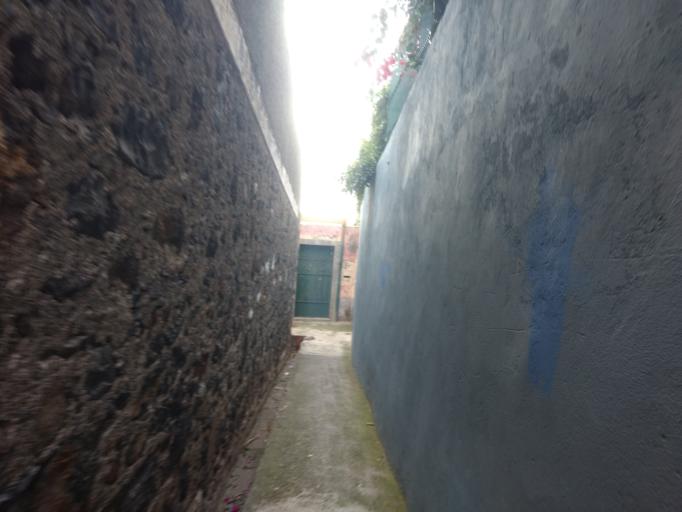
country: PT
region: Madeira
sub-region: Funchal
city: Funchal
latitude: 32.6466
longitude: -16.9212
